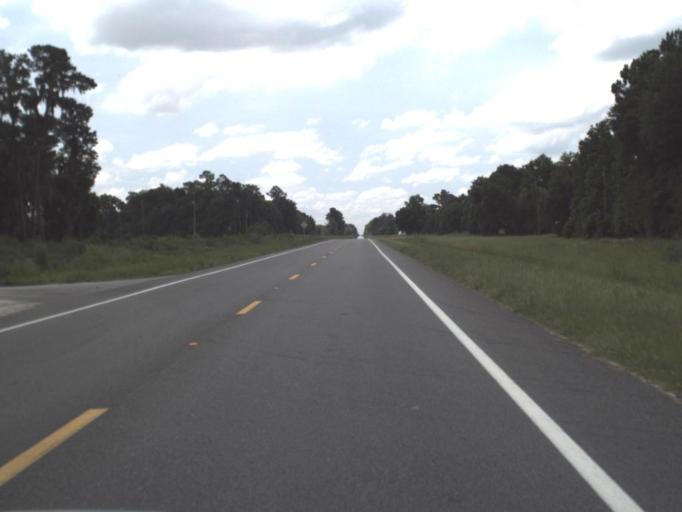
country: US
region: Florida
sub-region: Hamilton County
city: Jasper
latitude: 30.4763
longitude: -82.9128
